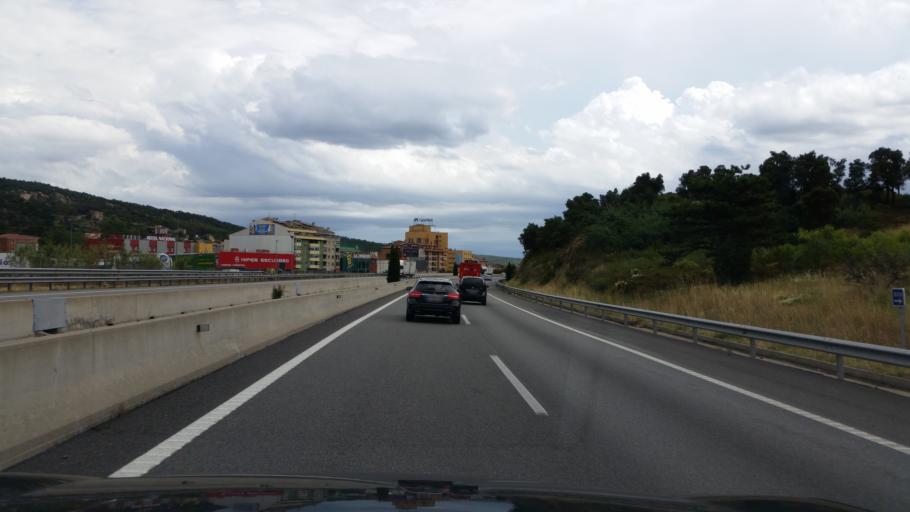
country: ES
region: Catalonia
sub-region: Provincia de Girona
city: la Jonquera
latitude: 42.4234
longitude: 2.8685
